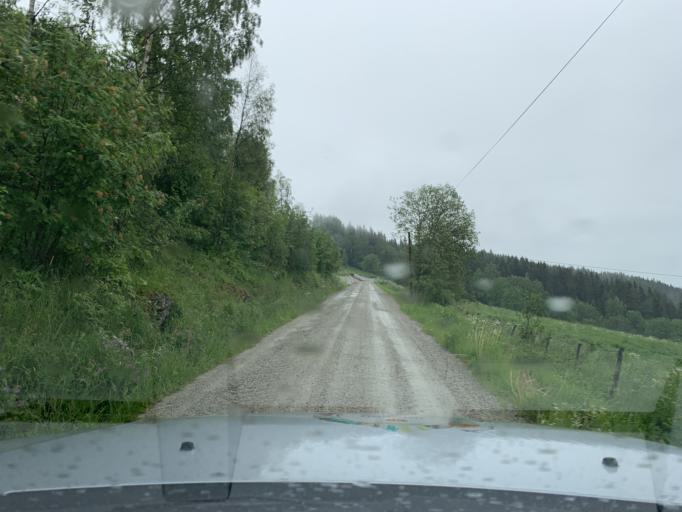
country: NO
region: Oppland
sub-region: Oyer
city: Tretten
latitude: 61.3879
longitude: 10.2808
